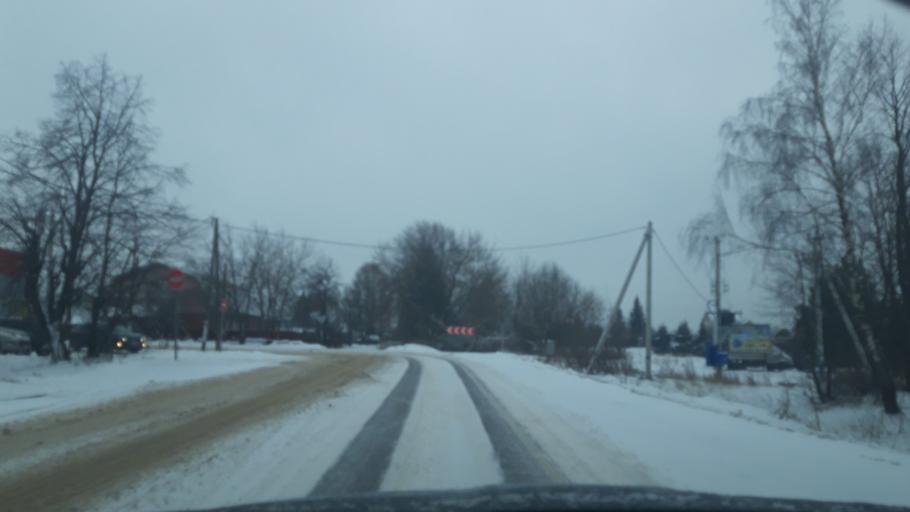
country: RU
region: Moskovskaya
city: Yakhroma
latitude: 56.2933
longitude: 37.4645
